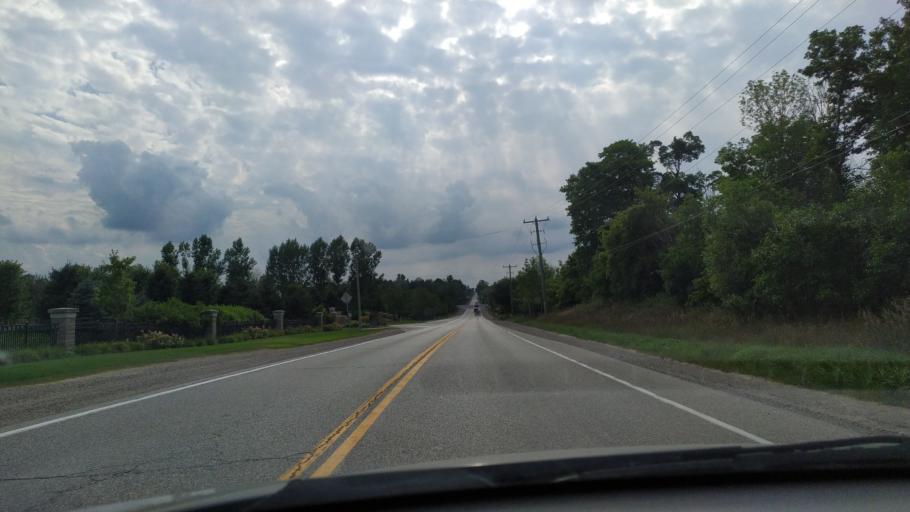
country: CA
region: Ontario
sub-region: Wellington County
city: Guelph
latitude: 43.4582
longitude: -80.1751
